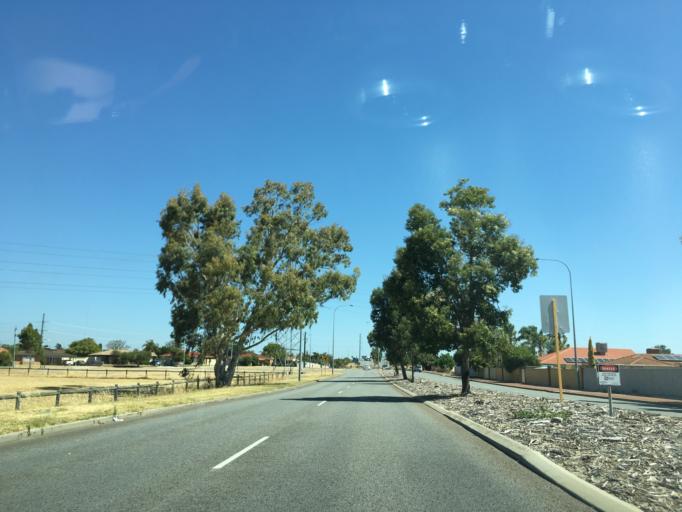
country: AU
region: Western Australia
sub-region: Canning
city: Canning Vale
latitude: -32.0524
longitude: 115.9044
